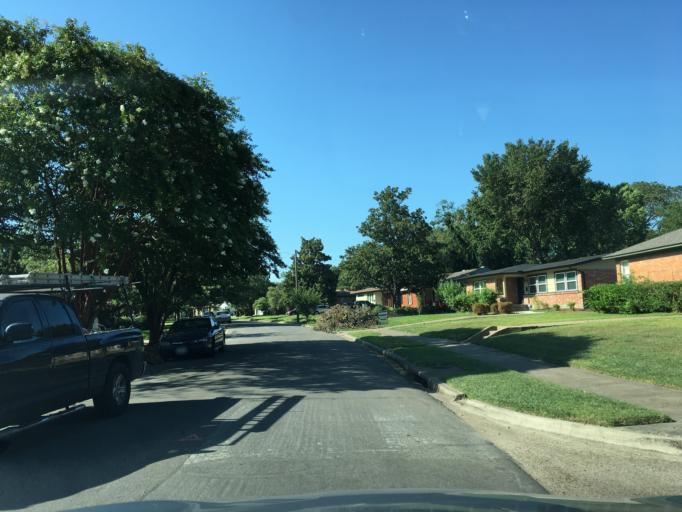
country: US
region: Texas
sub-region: Dallas County
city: Garland
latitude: 32.8634
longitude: -96.7083
